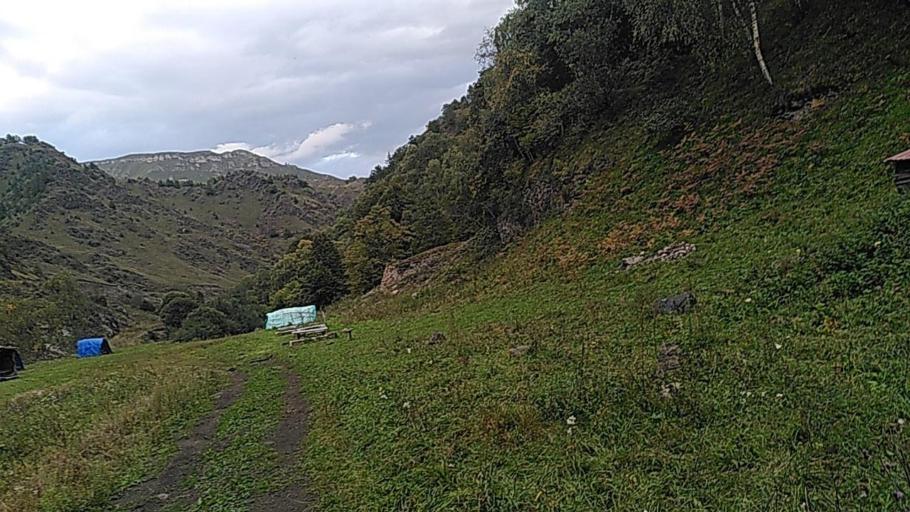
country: RU
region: Kabardino-Balkariya
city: Kamennomostskoye
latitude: 43.7190
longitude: 42.8428
